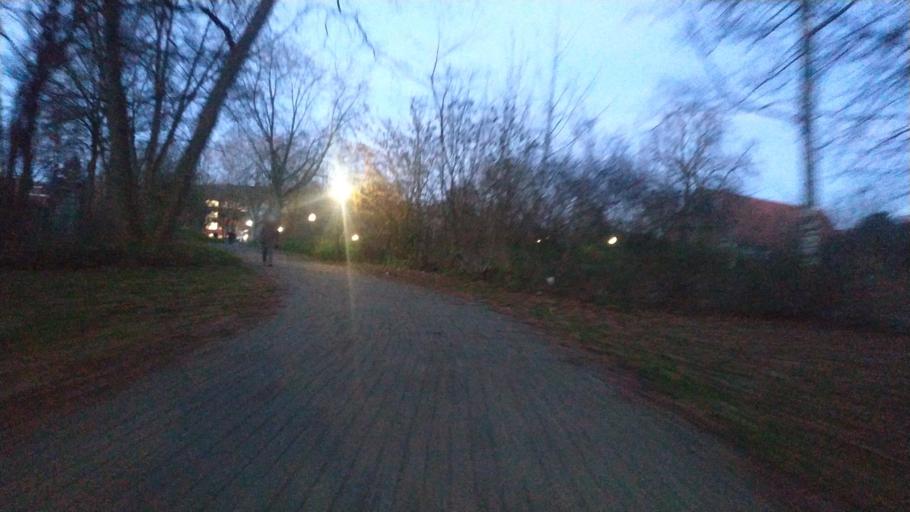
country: DE
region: North Rhine-Westphalia
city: Ibbenburen
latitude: 52.2669
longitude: 7.7352
